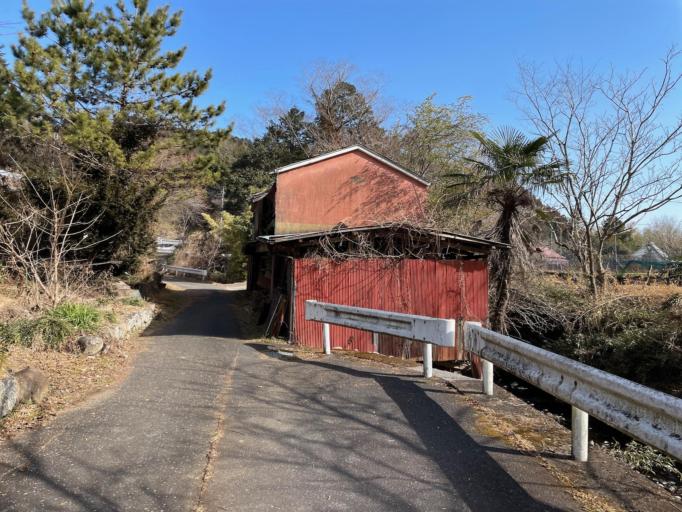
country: JP
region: Saitama
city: Hanno
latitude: 35.8447
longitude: 139.2636
